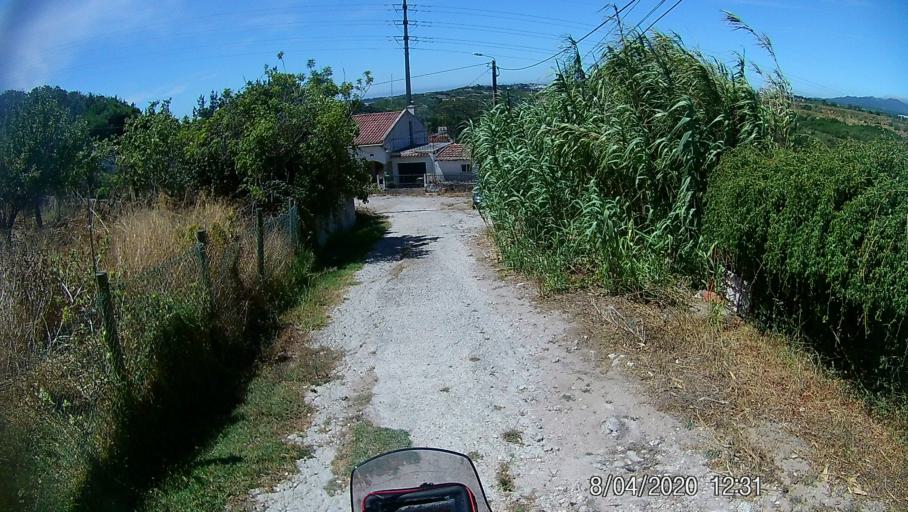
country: PT
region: Lisbon
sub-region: Sintra
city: Rio de Mouro
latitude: 38.7519
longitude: -9.3639
